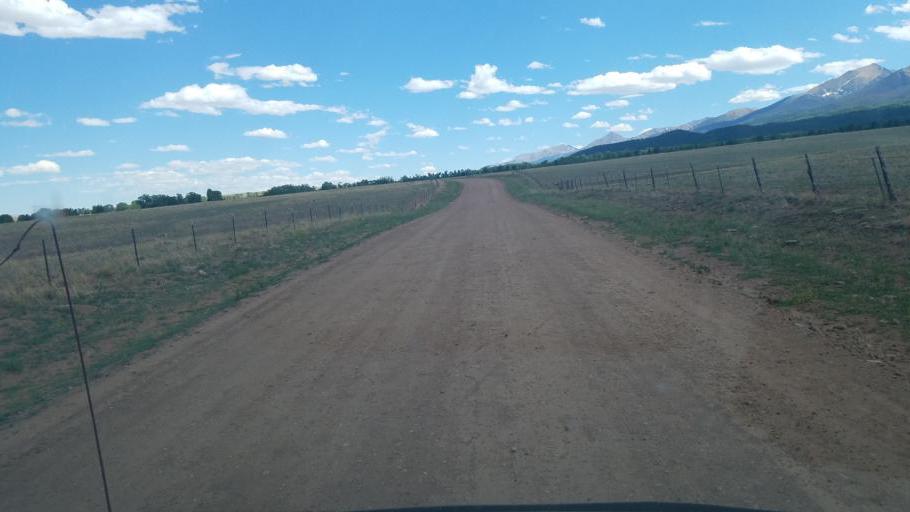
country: US
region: Colorado
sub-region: Custer County
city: Westcliffe
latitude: 38.2464
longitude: -105.6087
